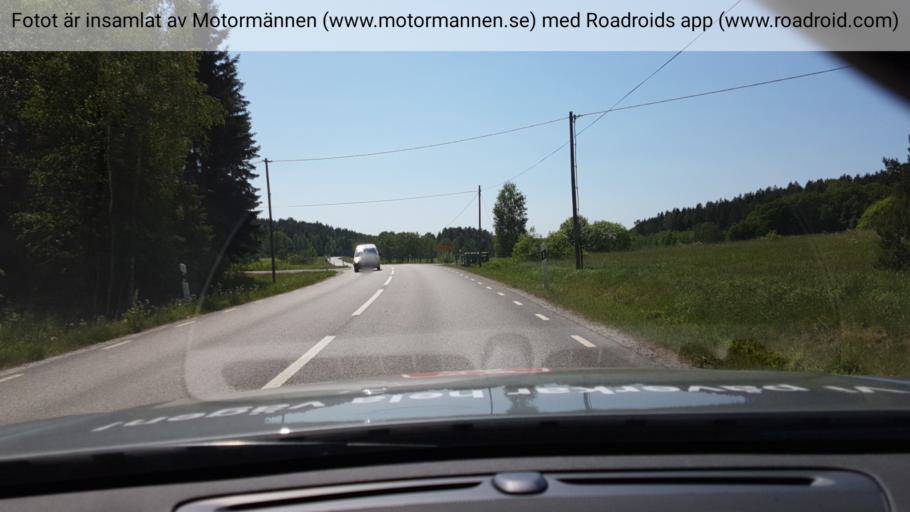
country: SE
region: Stockholm
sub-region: Norrtalje Kommun
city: Rimbo
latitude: 59.6602
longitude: 18.3415
